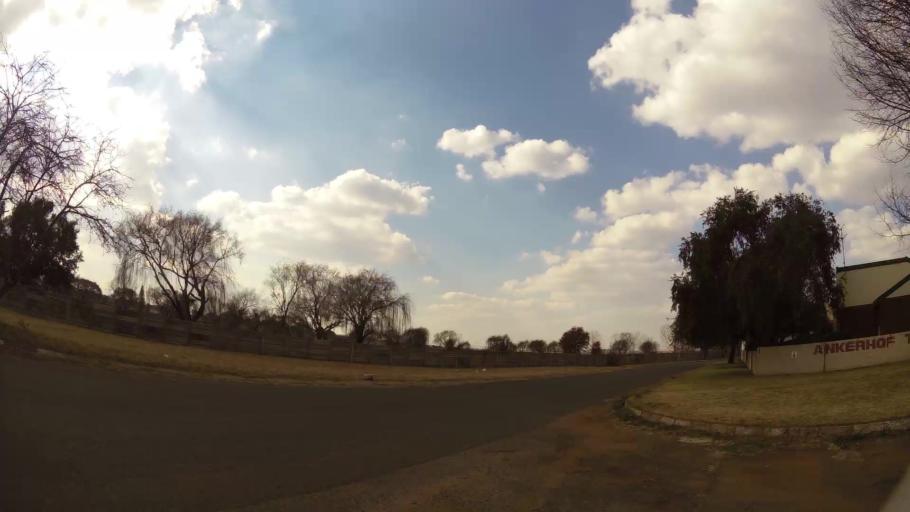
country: ZA
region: Mpumalanga
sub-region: Nkangala District Municipality
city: Delmas
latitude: -26.1441
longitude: 28.6819
